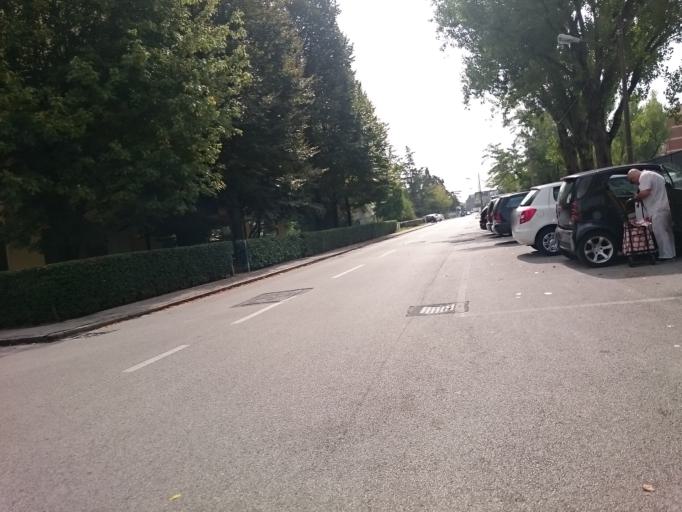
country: IT
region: Veneto
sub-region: Provincia di Padova
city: Padova
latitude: 45.4147
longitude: 11.9076
